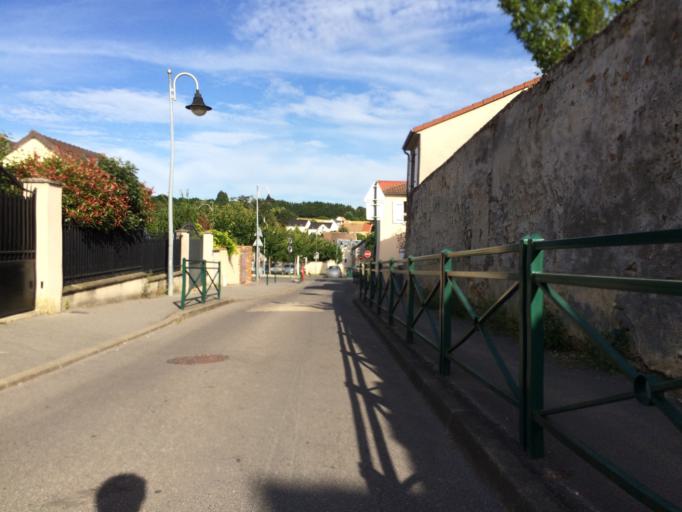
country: FR
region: Ile-de-France
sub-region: Departement de l'Essonne
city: Saulx-les-Chartreux
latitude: 48.6899
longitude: 2.2771
